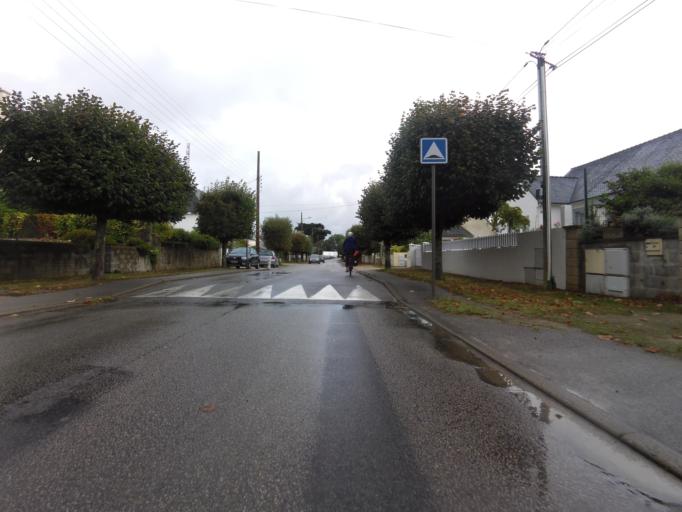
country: FR
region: Brittany
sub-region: Departement du Morbihan
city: Etel
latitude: 47.6618
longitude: -3.2043
